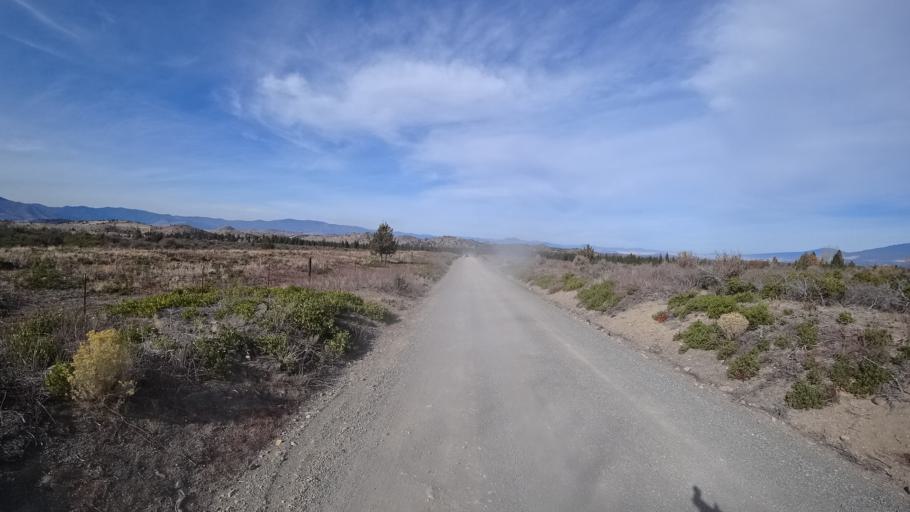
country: US
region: California
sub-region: Siskiyou County
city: Weed
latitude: 41.4837
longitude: -122.3654
